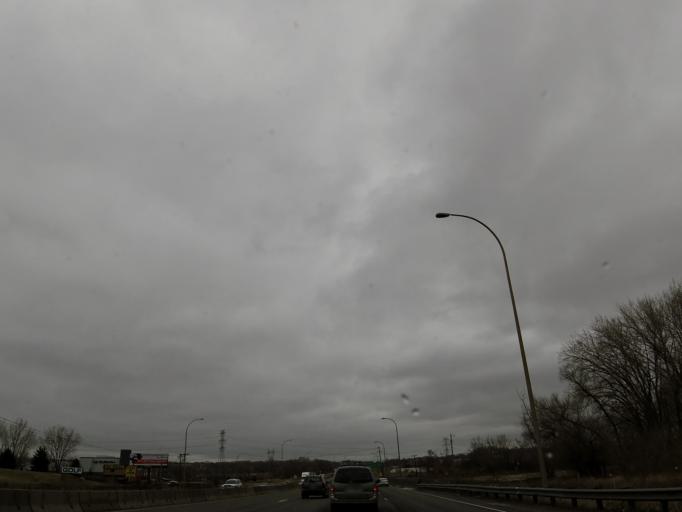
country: US
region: Minnesota
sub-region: Dakota County
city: Burnsville
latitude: 44.7882
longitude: -93.2890
